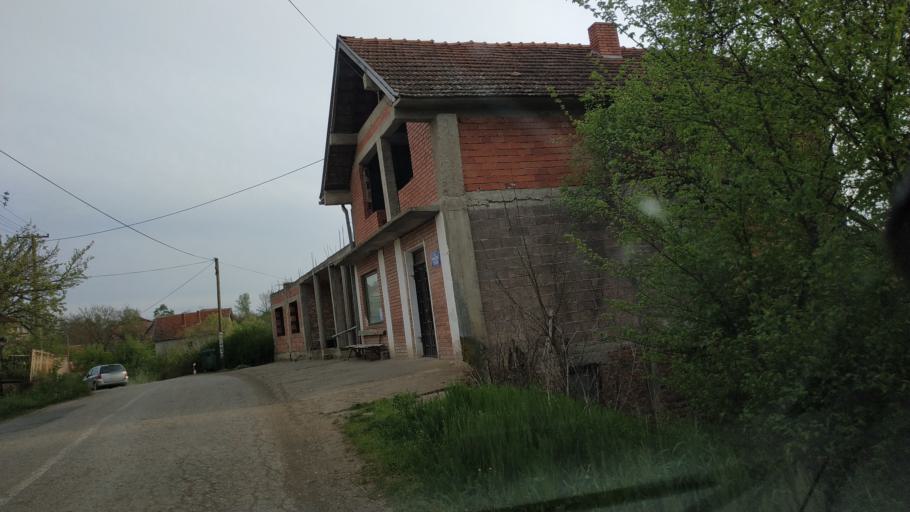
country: RS
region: Central Serbia
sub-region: Nisavski Okrug
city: Aleksinac
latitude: 43.4849
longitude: 21.8179
